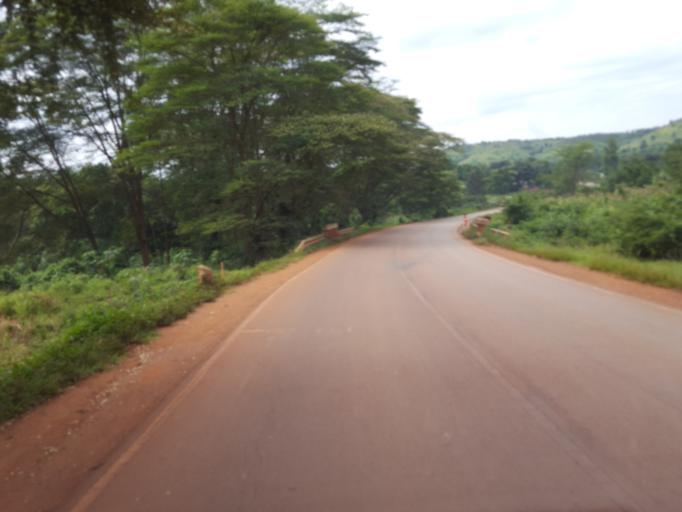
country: UG
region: Central Region
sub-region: Mityana District
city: Mityana
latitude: 0.6309
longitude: 32.1149
